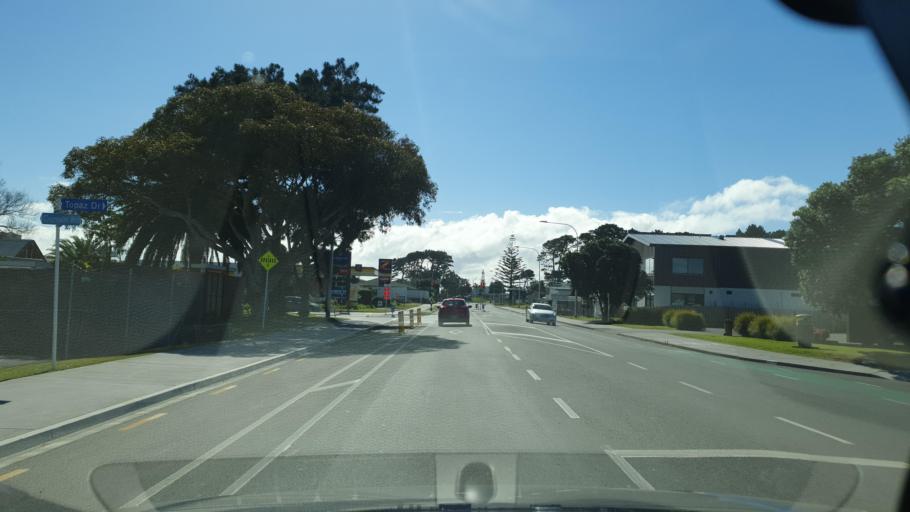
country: NZ
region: Bay of Plenty
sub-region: Tauranga City
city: Tauranga
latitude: -37.7001
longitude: 176.2847
